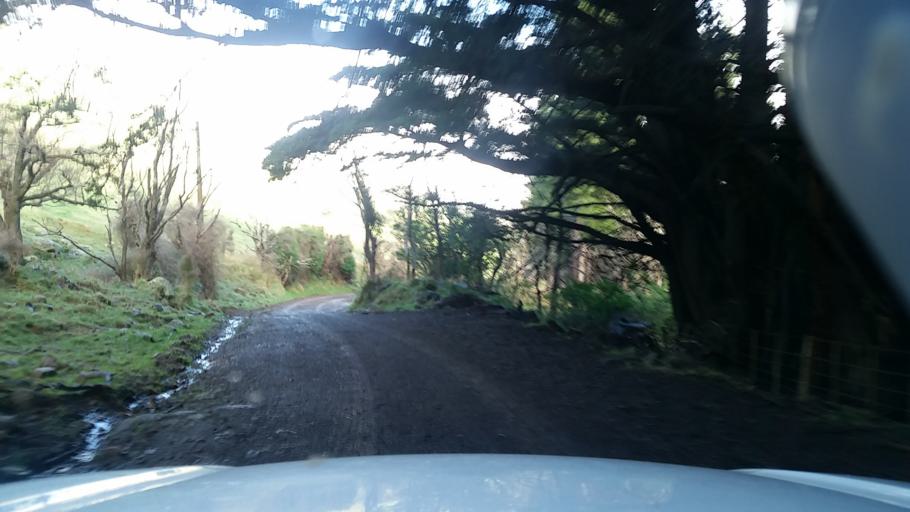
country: NZ
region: Canterbury
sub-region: Christchurch City
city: Christchurch
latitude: -43.6892
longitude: 172.9252
